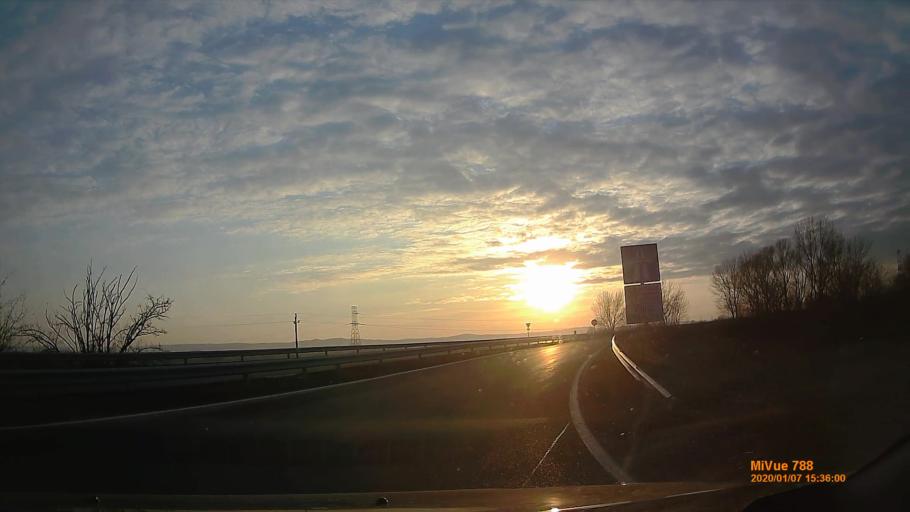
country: HU
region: Gyor-Moson-Sopron
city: Toltestava
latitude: 47.6479
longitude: 17.7126
